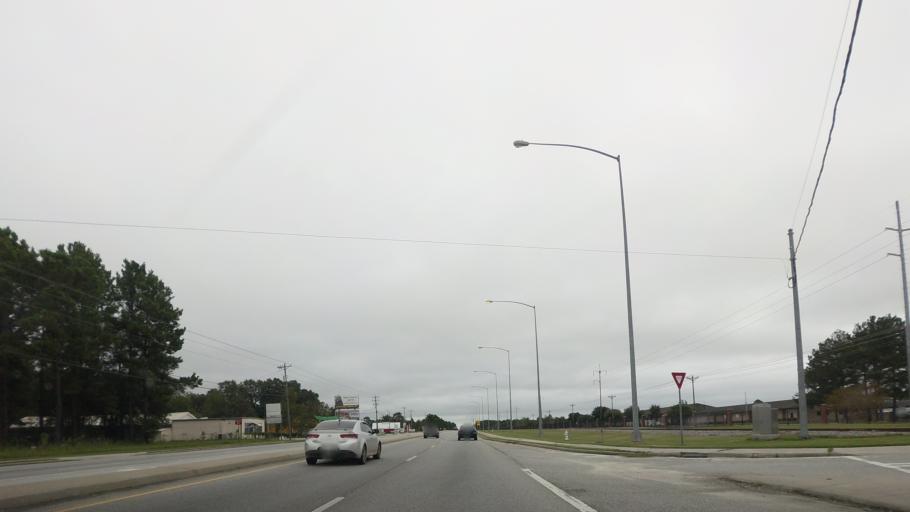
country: US
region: Georgia
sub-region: Berrien County
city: Ray City
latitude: 30.9711
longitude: -83.2149
